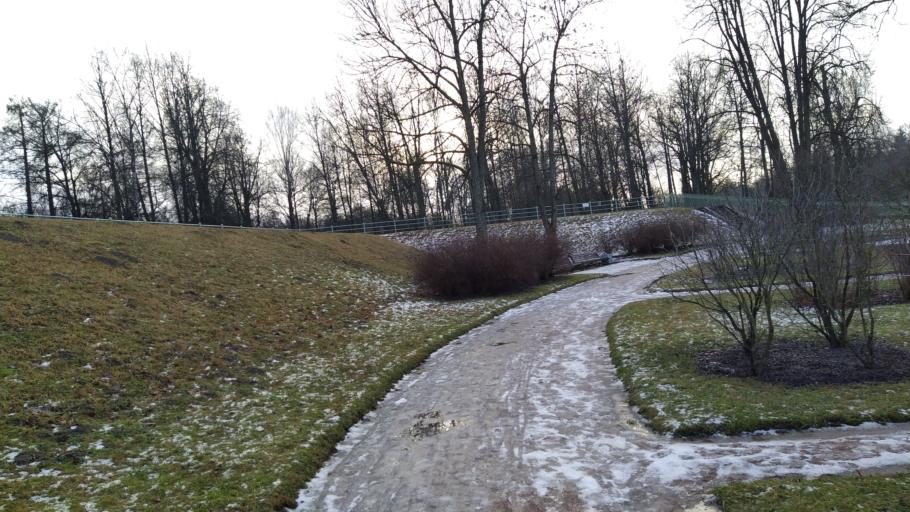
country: RU
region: St.-Petersburg
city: Pushkin
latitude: 59.7234
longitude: 30.3907
